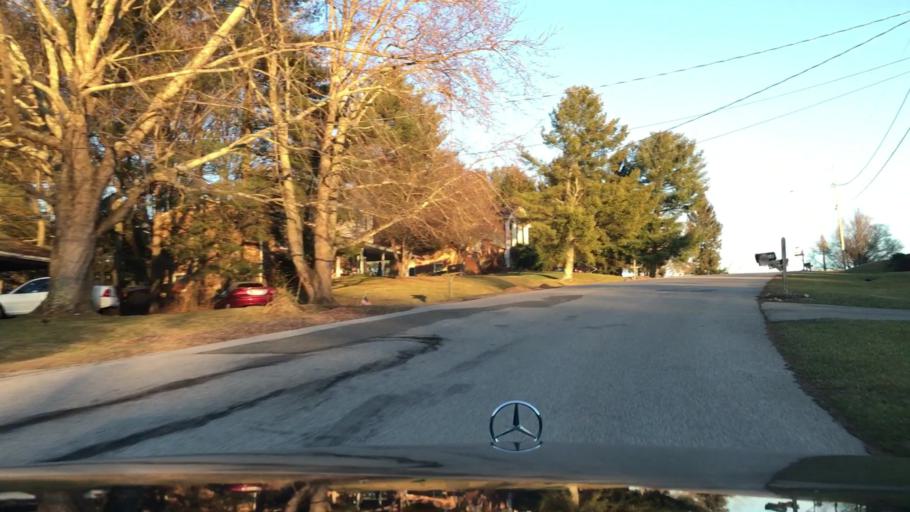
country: US
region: Virginia
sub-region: Montgomery County
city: Merrimac
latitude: 37.1667
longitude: -80.4431
